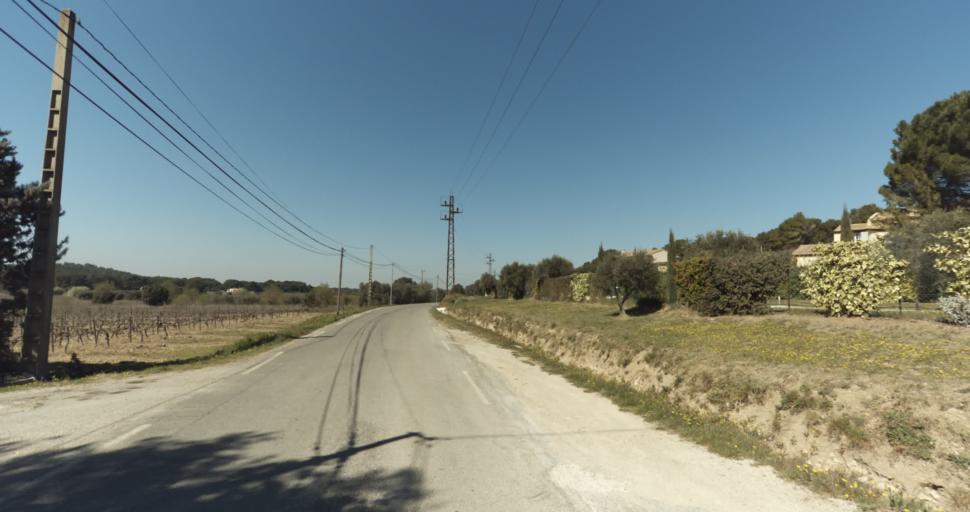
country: FR
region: Provence-Alpes-Cote d'Azur
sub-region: Departement des Bouches-du-Rhone
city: Pelissanne
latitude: 43.6097
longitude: 5.1788
